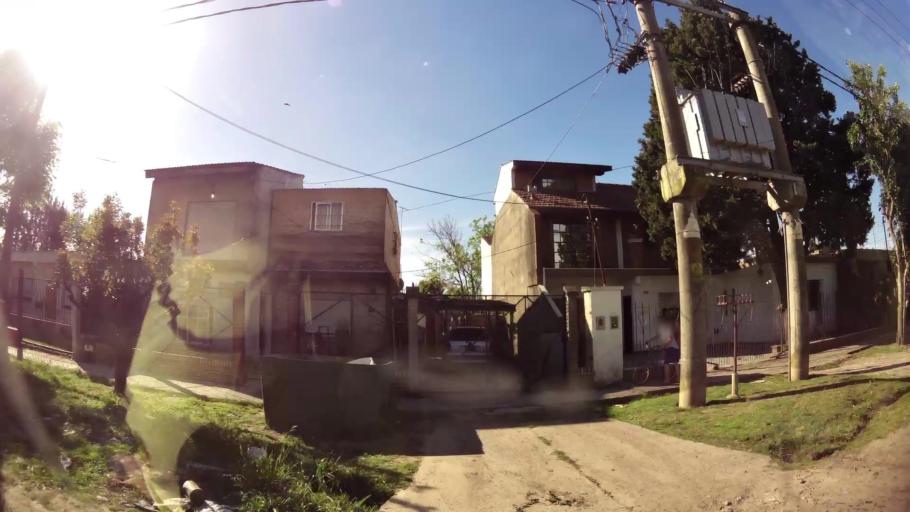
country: AR
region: Buenos Aires
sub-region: Partido de Almirante Brown
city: Adrogue
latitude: -34.8262
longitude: -58.3477
